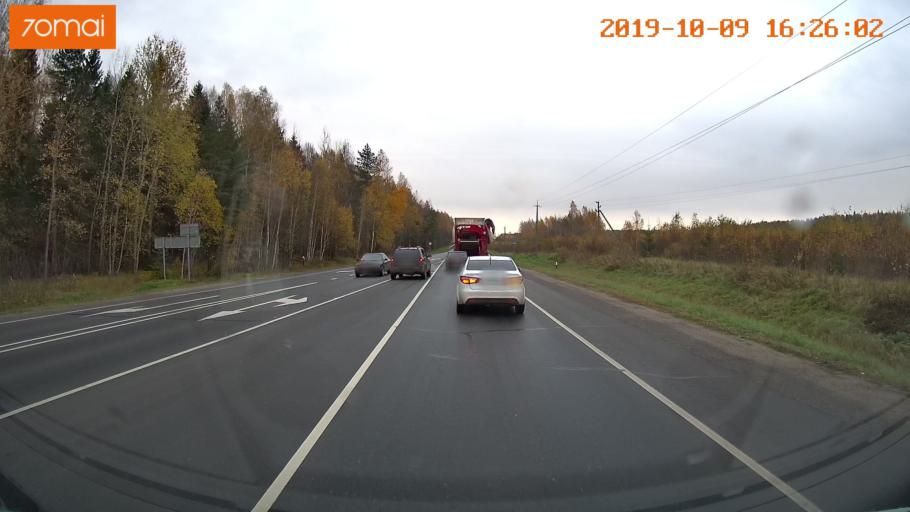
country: RU
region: Kostroma
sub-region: Kostromskoy Rayon
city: Kostroma
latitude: 57.6395
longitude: 40.9224
